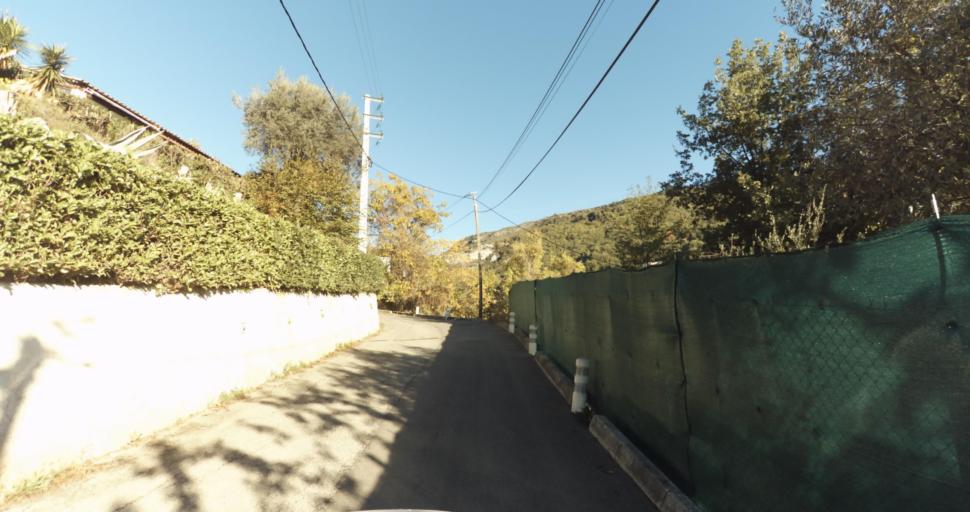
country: FR
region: Provence-Alpes-Cote d'Azur
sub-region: Departement des Alpes-Maritimes
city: Vence
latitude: 43.7293
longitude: 7.0848
